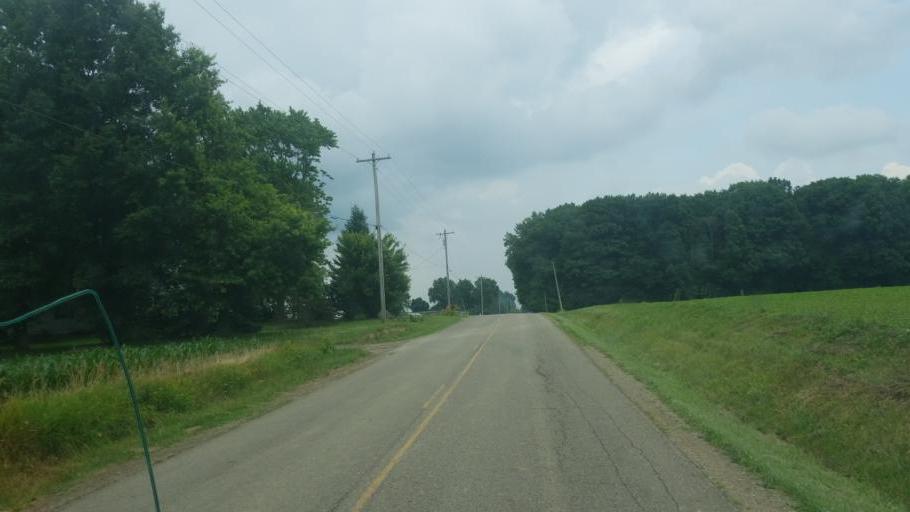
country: US
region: Ohio
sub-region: Wayne County
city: Smithville
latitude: 40.9014
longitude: -81.8920
